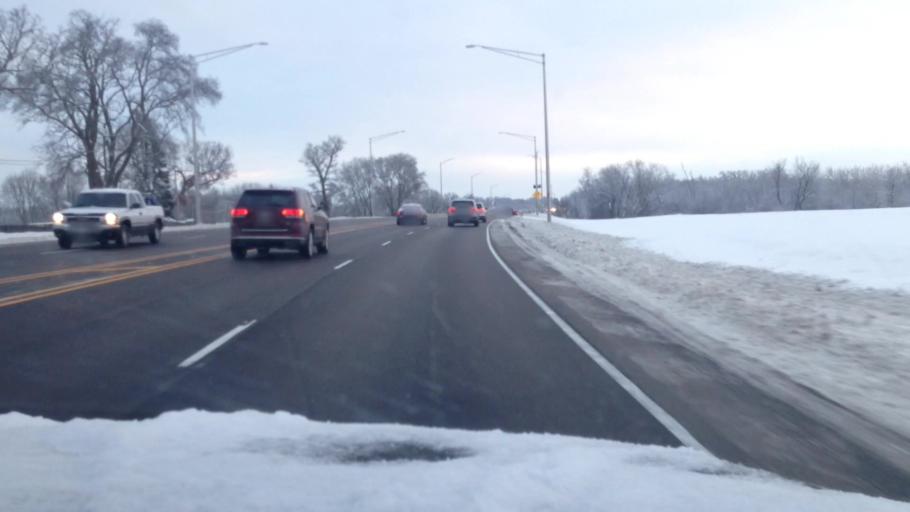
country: US
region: Illinois
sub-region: Kane County
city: Sleepy Hollow
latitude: 42.0615
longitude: -88.3362
